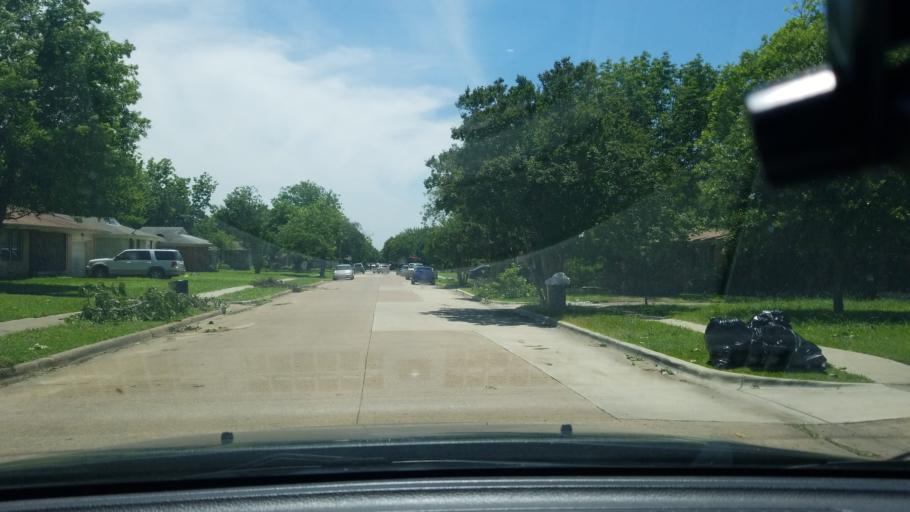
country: US
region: Texas
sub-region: Dallas County
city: Mesquite
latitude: 32.7861
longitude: -96.6137
